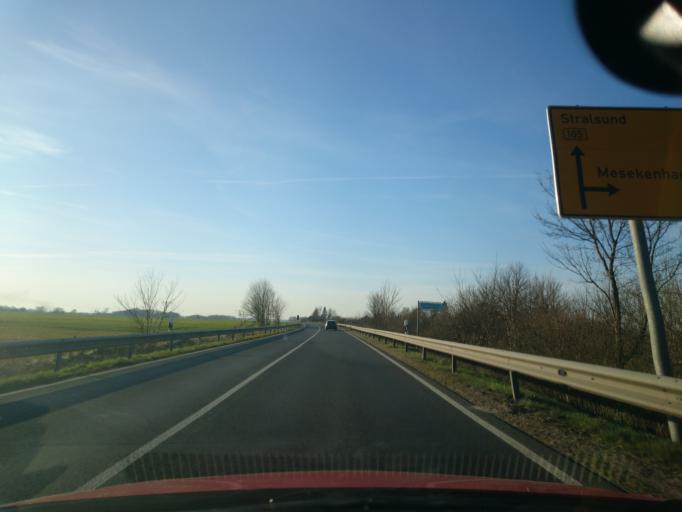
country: DE
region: Mecklenburg-Vorpommern
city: Mesekenhagen
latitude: 54.1406
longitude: 13.3313
